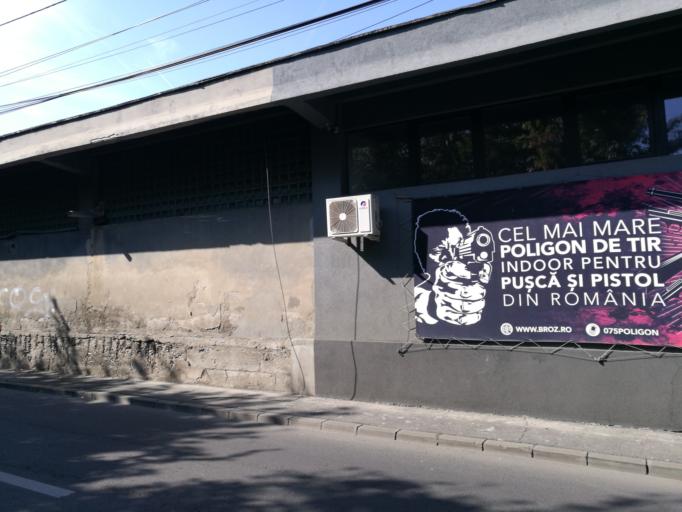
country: RO
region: Bucuresti
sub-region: Municipiul Bucuresti
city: Bucuresti
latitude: 44.4846
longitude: 26.0693
